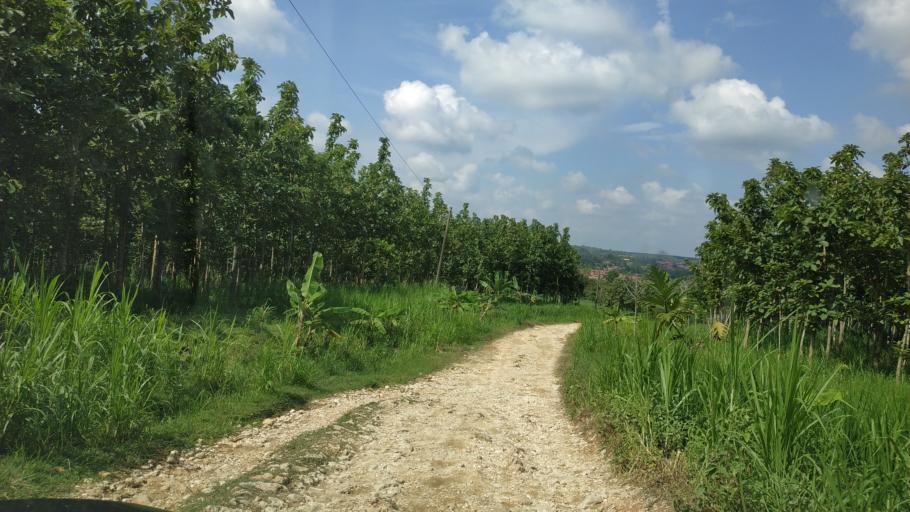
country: ID
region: Central Java
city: Guyangan
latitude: -7.0066
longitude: 111.0995
